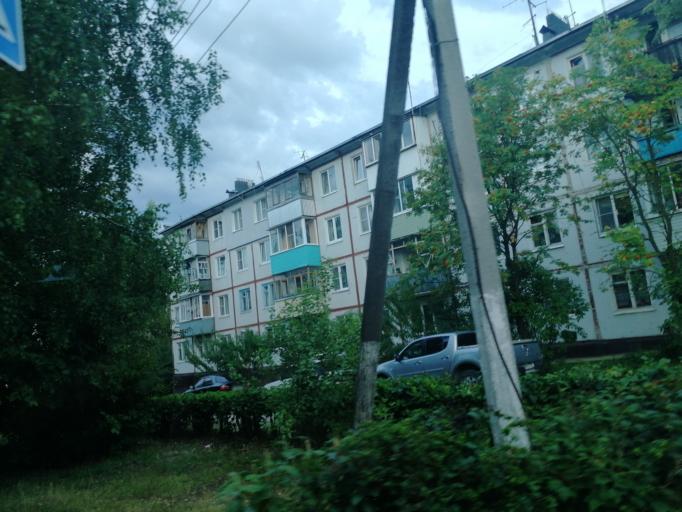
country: RU
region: Tula
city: Kosaya Gora
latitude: 54.1650
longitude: 37.4709
